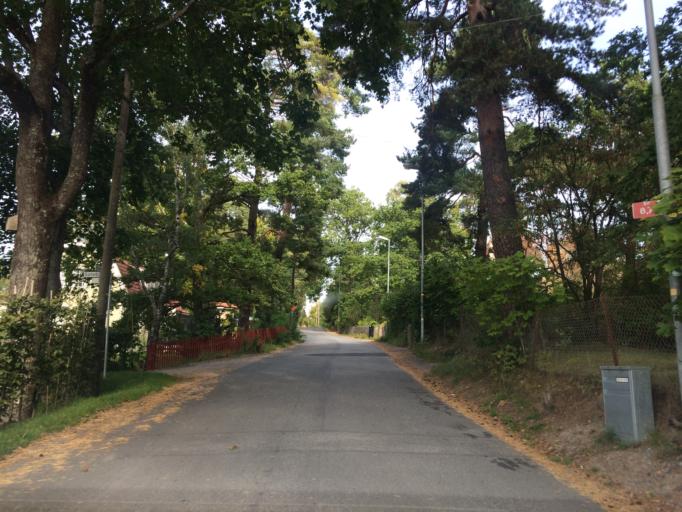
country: SE
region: Stockholm
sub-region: Sollentuna Kommun
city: Sollentuna
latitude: 59.4560
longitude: 17.9301
